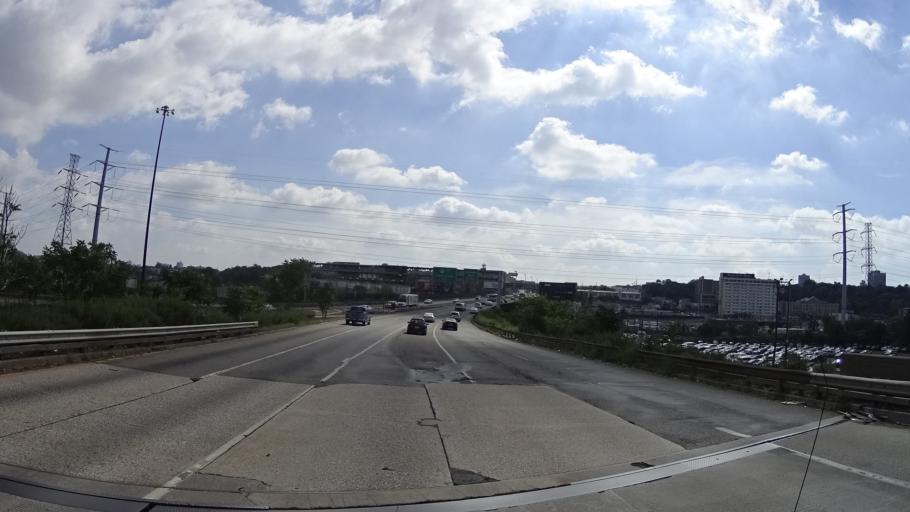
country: US
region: New Jersey
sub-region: Hudson County
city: Secaucus
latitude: 40.7771
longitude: -74.0452
